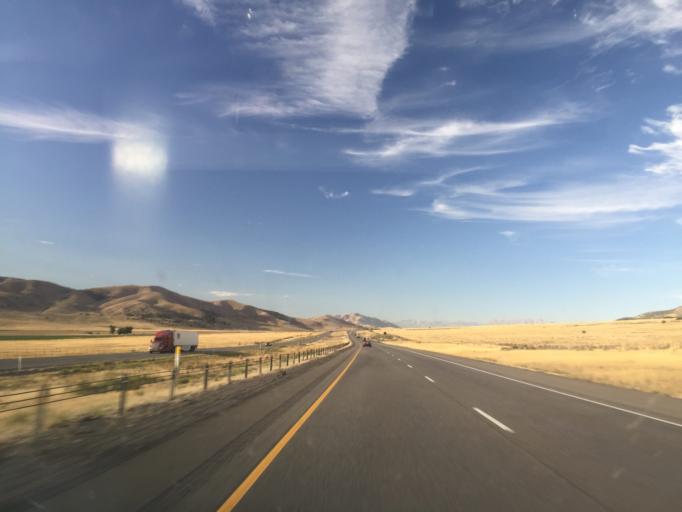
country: US
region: Utah
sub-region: Juab County
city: Mona
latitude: 39.8802
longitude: -111.8280
